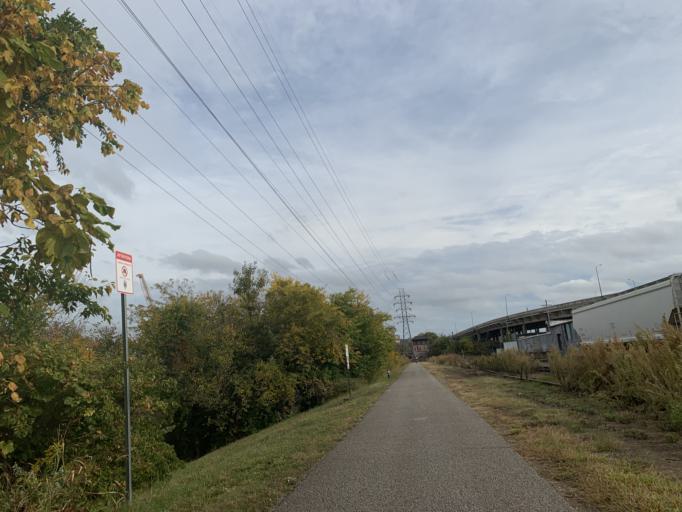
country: US
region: Kentucky
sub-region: Jefferson County
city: Louisville
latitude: 38.2655
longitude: -85.7745
